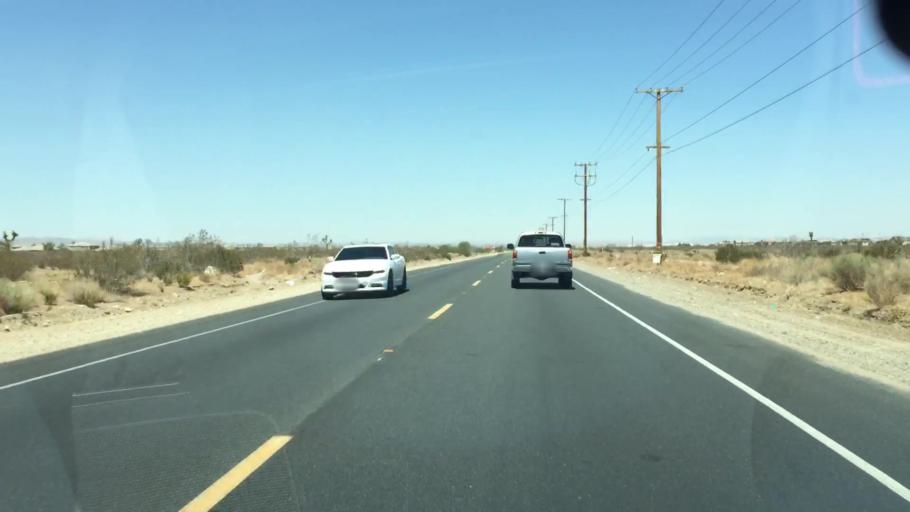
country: US
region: California
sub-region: San Bernardino County
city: Mountain View Acres
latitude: 34.4797
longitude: -117.3995
